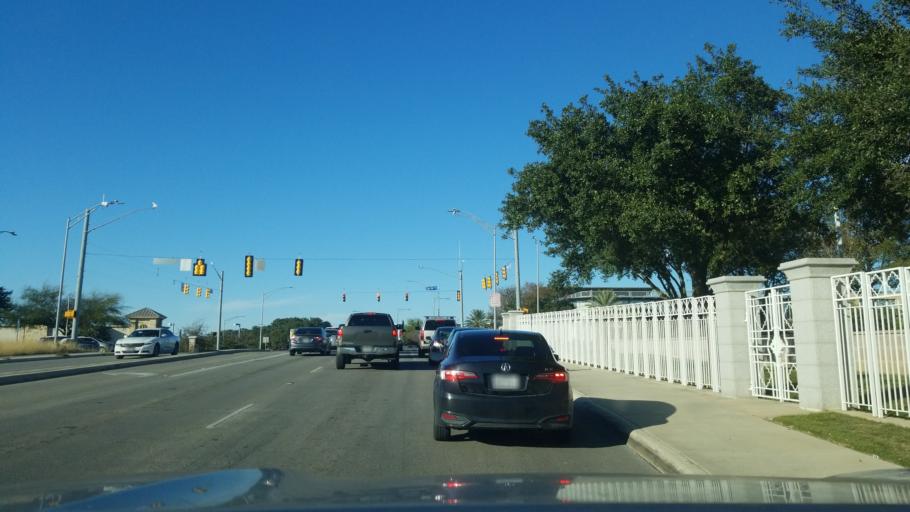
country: US
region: Texas
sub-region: Bexar County
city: Hollywood Park
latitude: 29.6415
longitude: -98.4892
